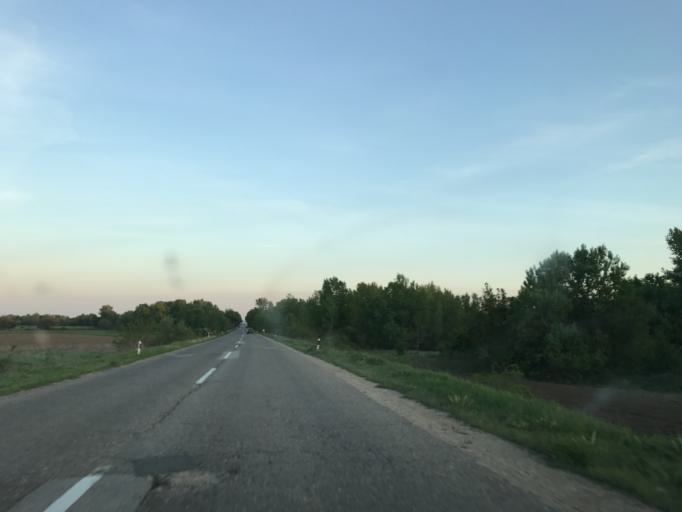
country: RS
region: Central Serbia
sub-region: Borski Okrug
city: Negotin
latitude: 44.2725
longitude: 22.5103
